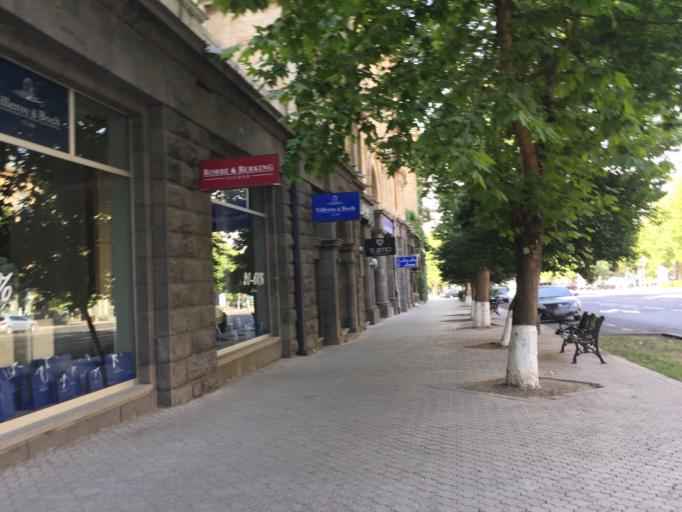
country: AM
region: Yerevan
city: Yerevan
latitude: 40.1890
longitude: 44.5175
